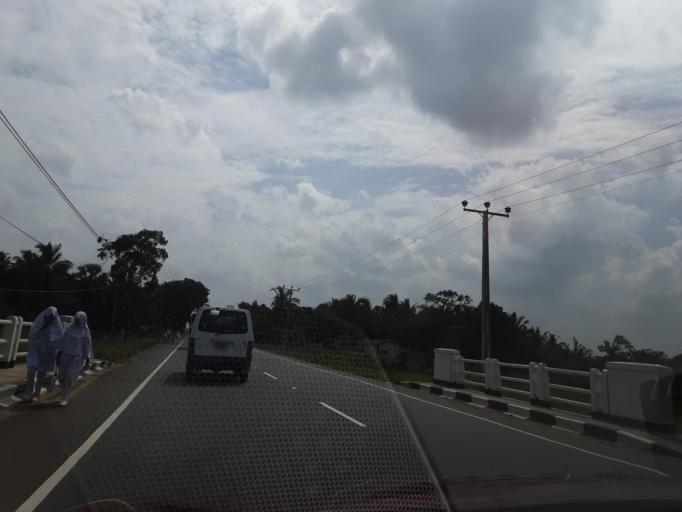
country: LK
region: North Central
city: Anuradhapura
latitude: 8.4739
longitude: 80.5127
